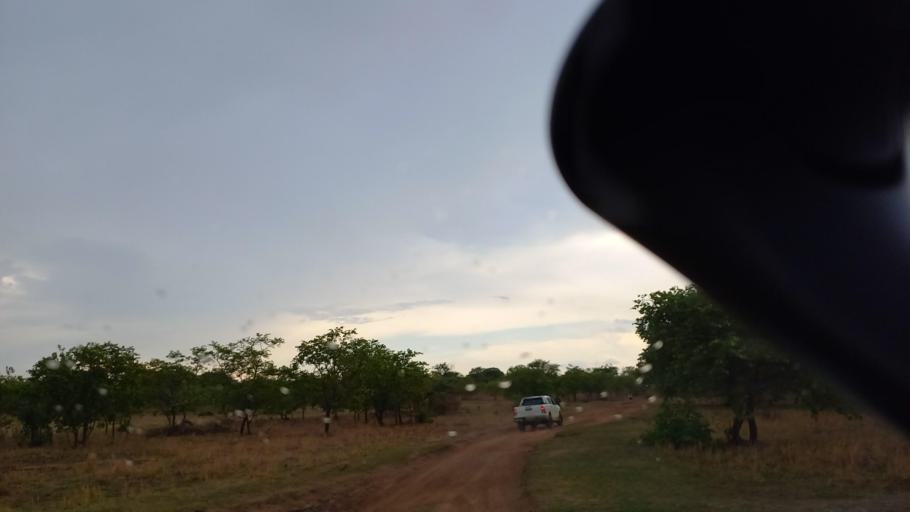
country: ZM
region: Lusaka
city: Kafue
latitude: -15.9822
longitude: 28.2603
